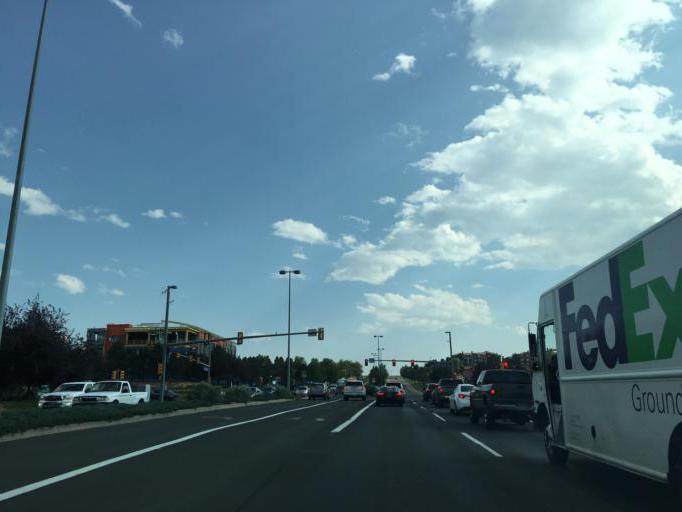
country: US
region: Colorado
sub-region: Broomfield County
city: Broomfield
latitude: 39.9298
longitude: -105.1279
